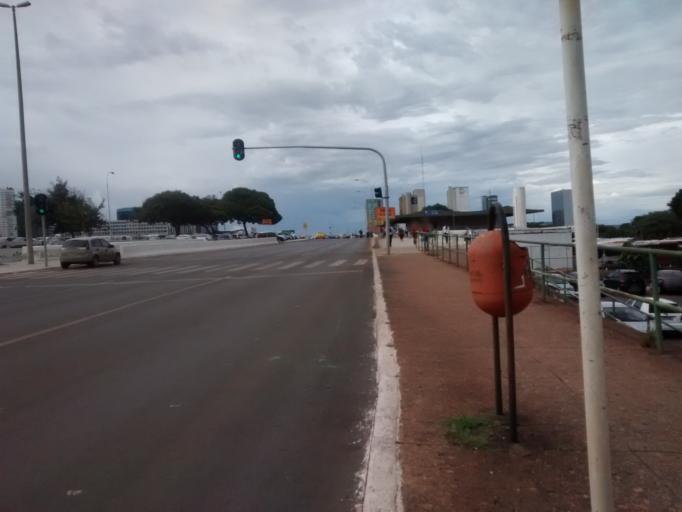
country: BR
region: Federal District
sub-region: Brasilia
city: Brasilia
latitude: -15.7979
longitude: -47.8834
